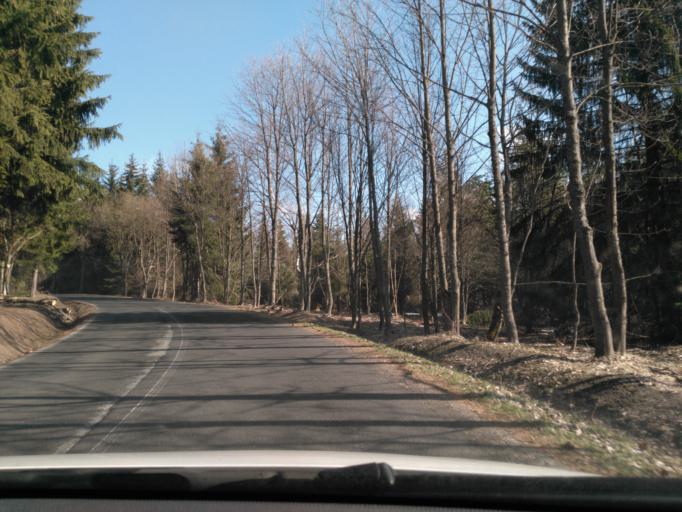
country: CZ
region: Ustecky
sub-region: Okres Chomutov
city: Kovarska
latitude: 50.4554
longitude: 13.0560
